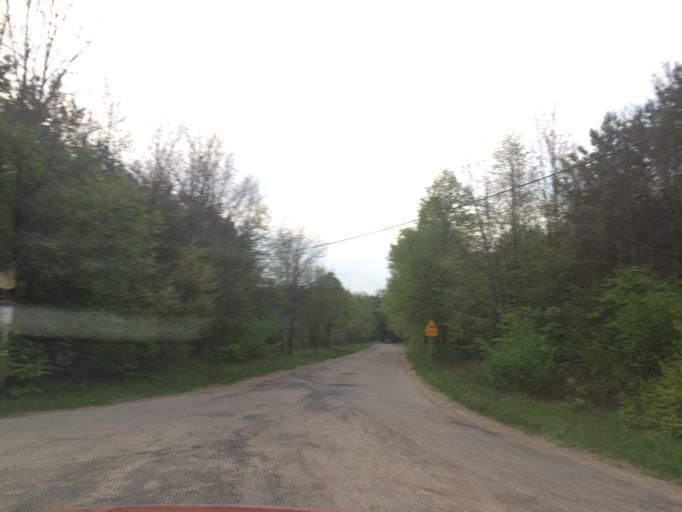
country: PL
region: Warmian-Masurian Voivodeship
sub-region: Powiat nowomiejski
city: Kurzetnik
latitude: 53.3703
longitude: 19.5211
